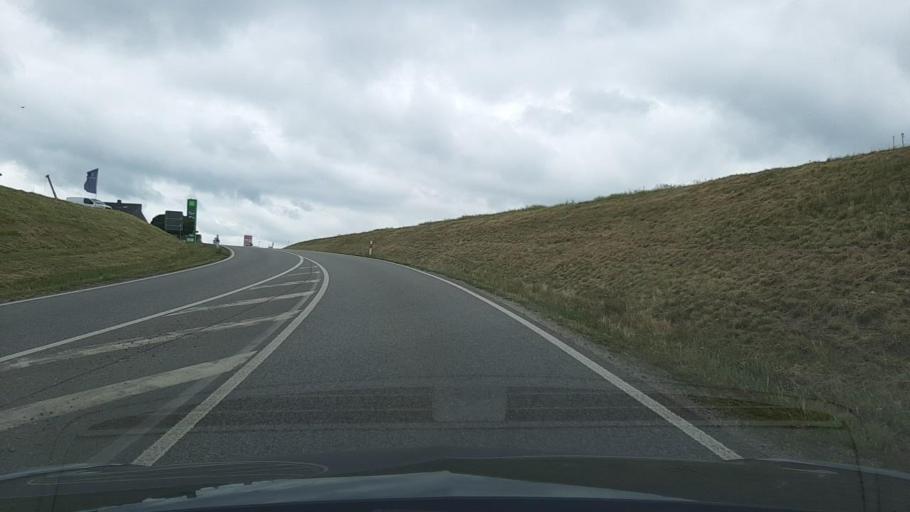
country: DE
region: Rheinland-Pfalz
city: Roth
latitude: 50.0804
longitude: 7.4577
